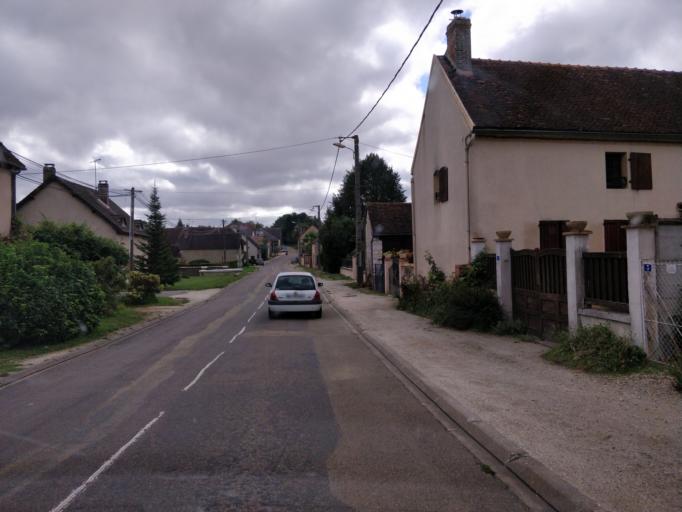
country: FR
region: Bourgogne
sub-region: Departement de l'Yonne
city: Saint-Florentin
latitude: 48.0855
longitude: 3.6974
